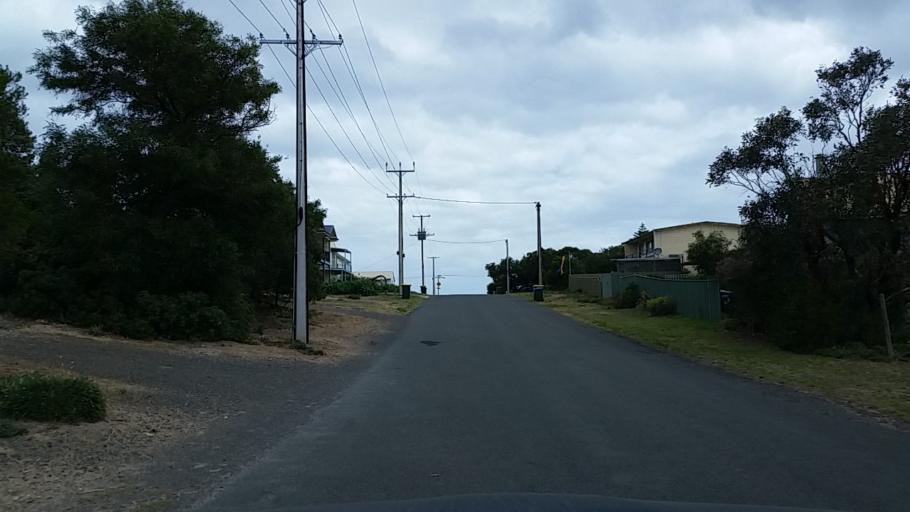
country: AU
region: South Australia
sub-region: Alexandrina
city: Port Elliot
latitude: -35.5340
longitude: 138.6692
